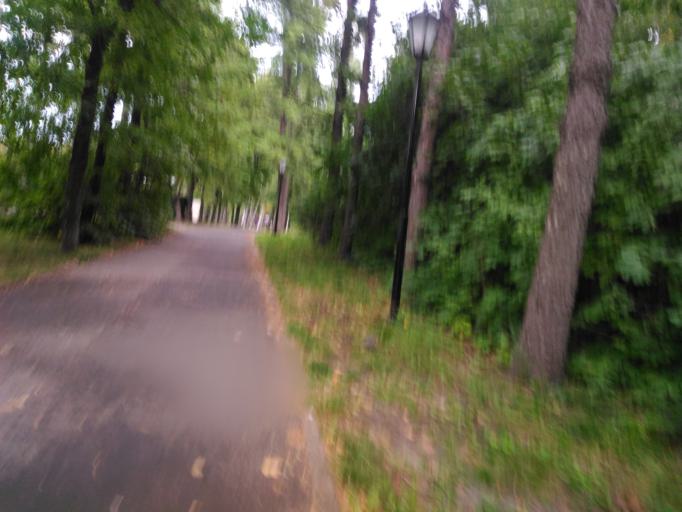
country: RU
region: Ulyanovsk
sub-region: Ulyanovskiy Rayon
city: Ulyanovsk
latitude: 54.2716
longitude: 48.3356
